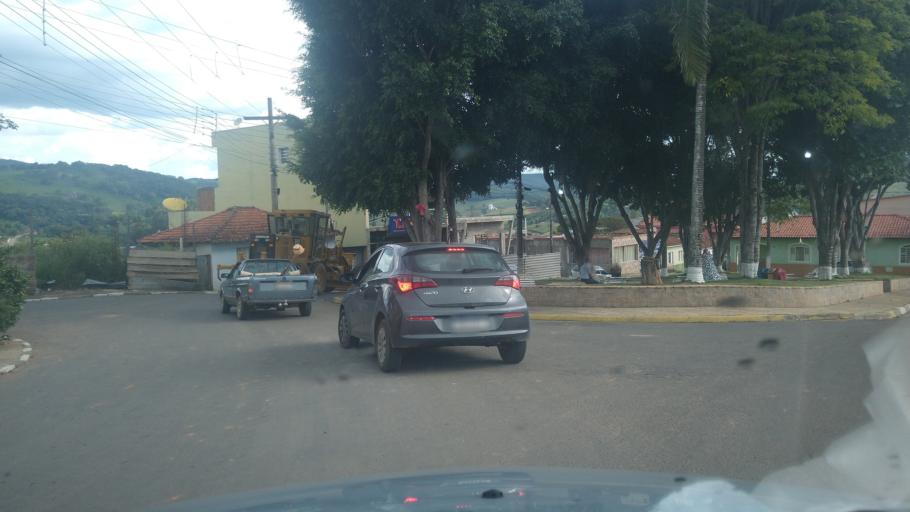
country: BR
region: Minas Gerais
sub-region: Extrema
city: Extrema
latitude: -22.7409
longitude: -46.3712
